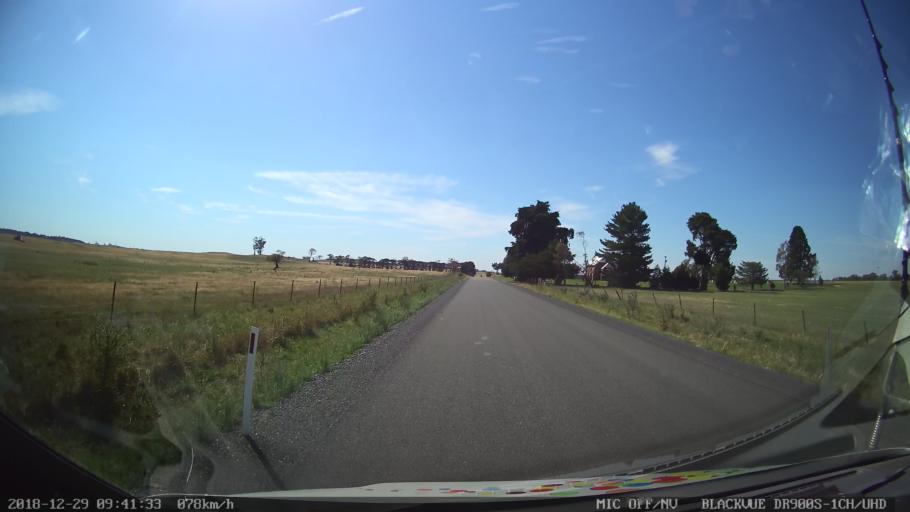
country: AU
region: New South Wales
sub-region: Upper Lachlan Shire
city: Crookwell
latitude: -34.6616
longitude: 149.4124
